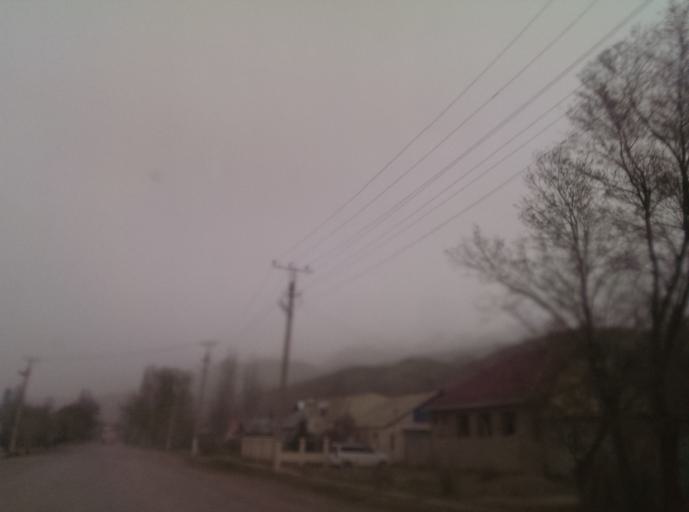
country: KG
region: Naryn
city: Naryn
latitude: 41.4235
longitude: 76.0143
